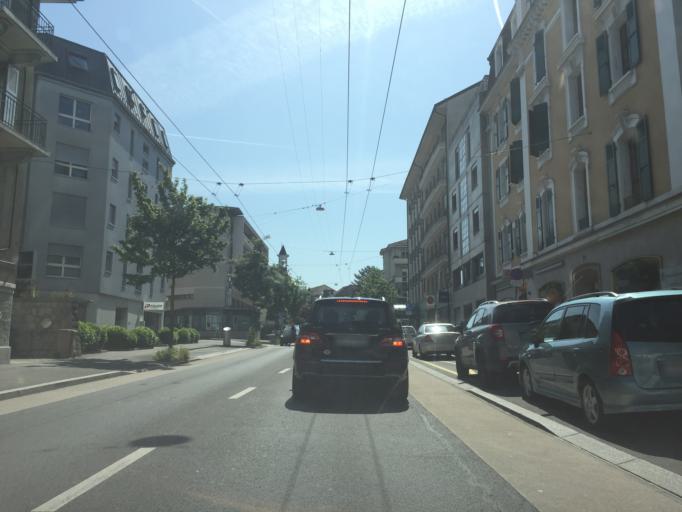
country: CH
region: Vaud
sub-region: Lausanne District
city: Lausanne
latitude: 46.5163
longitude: 6.6132
